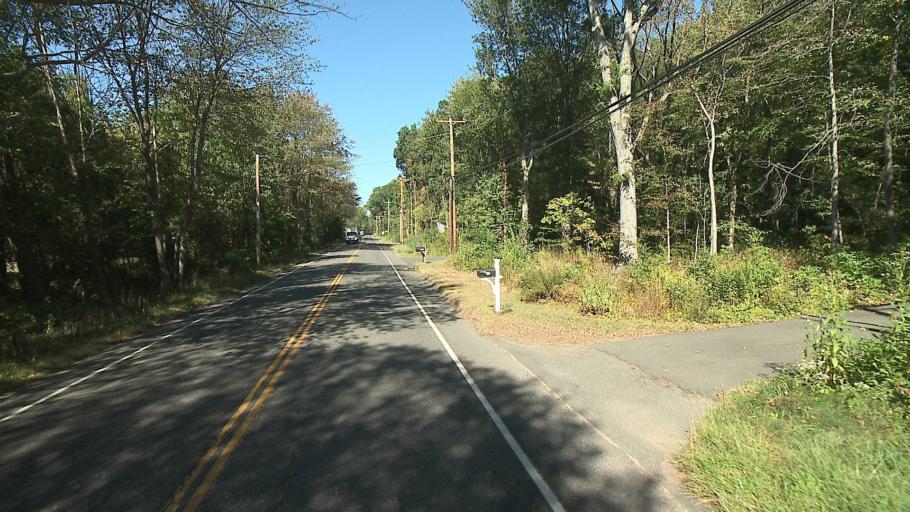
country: US
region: Connecticut
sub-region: New Haven County
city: Woodbridge
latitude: 41.3206
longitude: -73.0232
